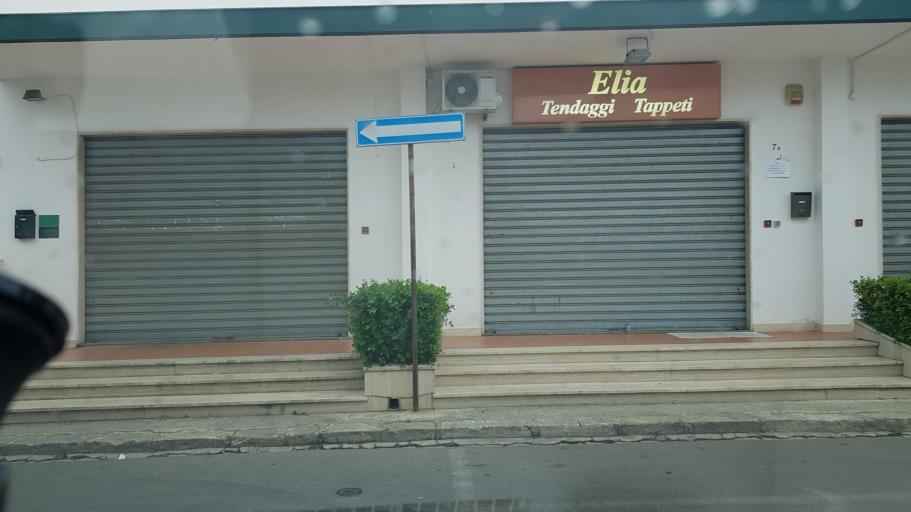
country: IT
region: Apulia
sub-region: Provincia di Lecce
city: Leverano
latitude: 40.2898
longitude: 17.9960
